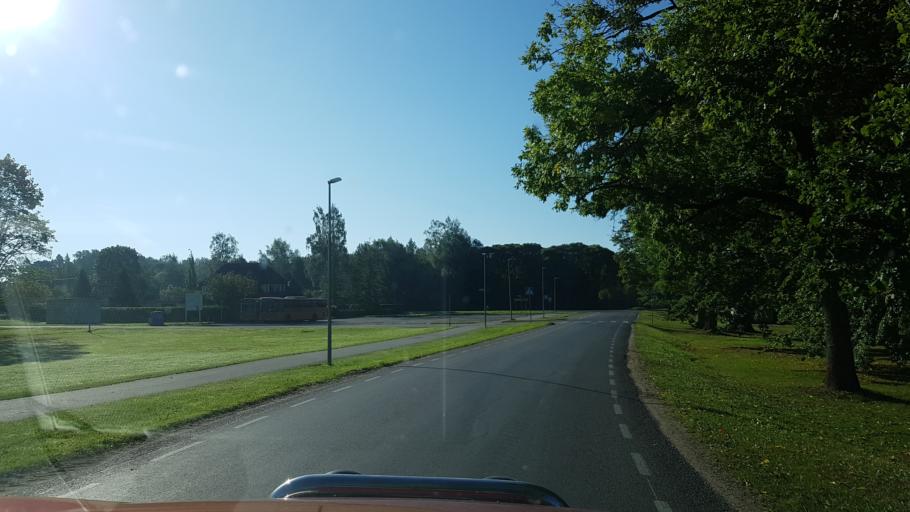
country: EE
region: Jogevamaa
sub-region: Tabivere vald
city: Tabivere
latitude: 58.6849
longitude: 26.5848
